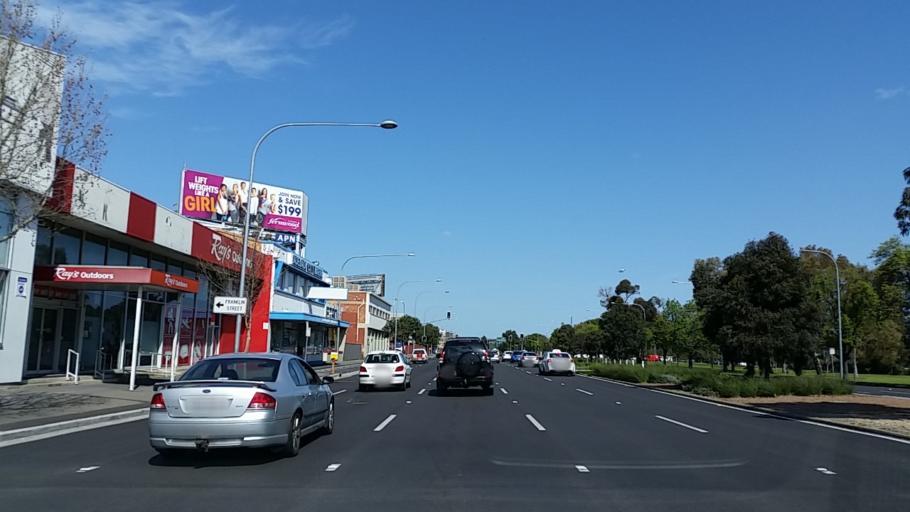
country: AU
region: South Australia
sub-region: Adelaide
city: Adelaide
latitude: -34.9265
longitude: 138.5878
